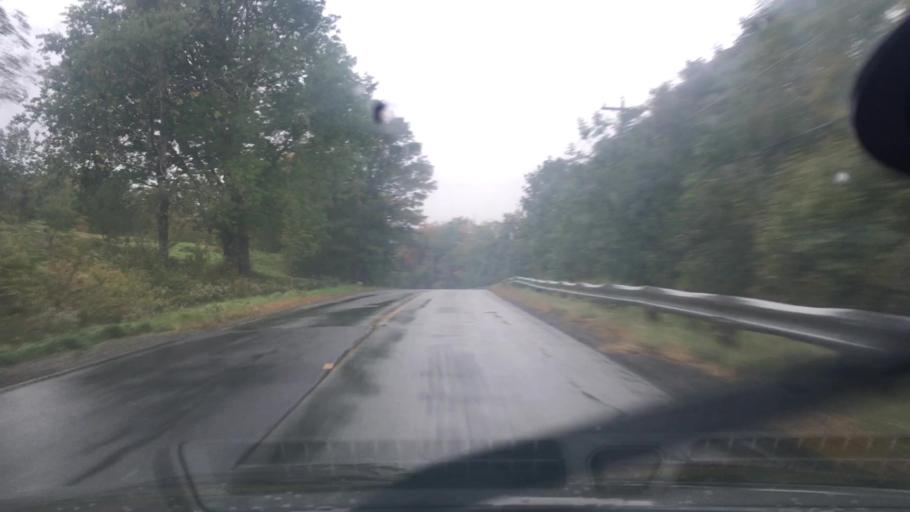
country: CA
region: Nova Scotia
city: Windsor
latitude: 44.8334
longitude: -64.2594
